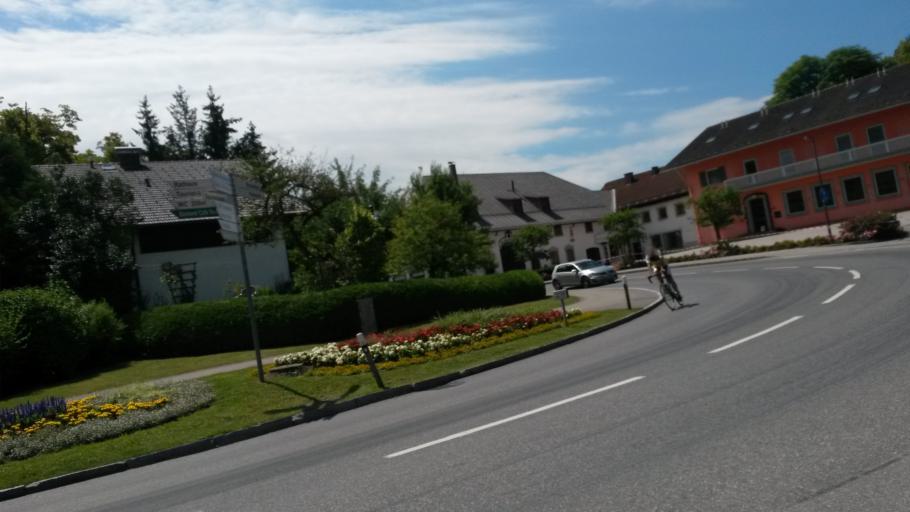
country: DE
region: Bavaria
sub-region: Upper Bavaria
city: Chieming
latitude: 47.8904
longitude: 12.5344
